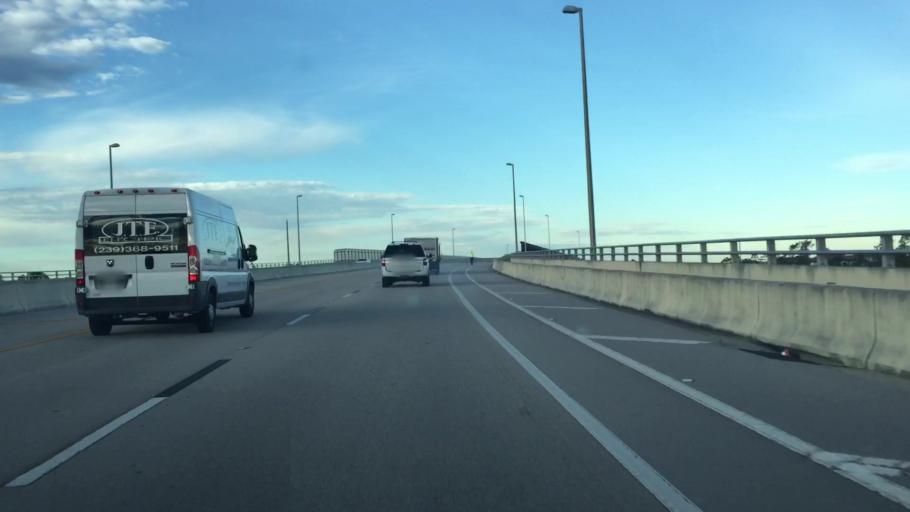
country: US
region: Florida
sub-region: Lee County
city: Three Oaks
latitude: 26.4490
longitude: -81.7816
